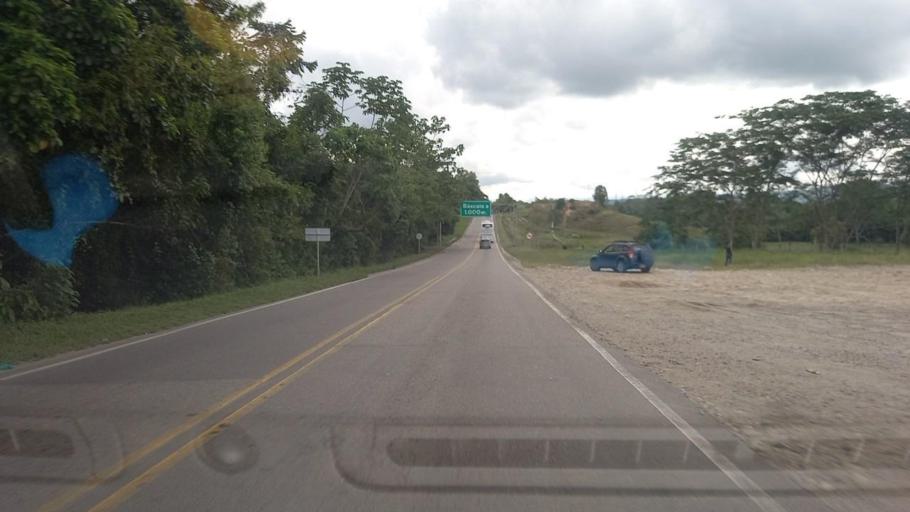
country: CO
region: Santander
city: Barrancabermeja
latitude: 7.1212
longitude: -73.5953
